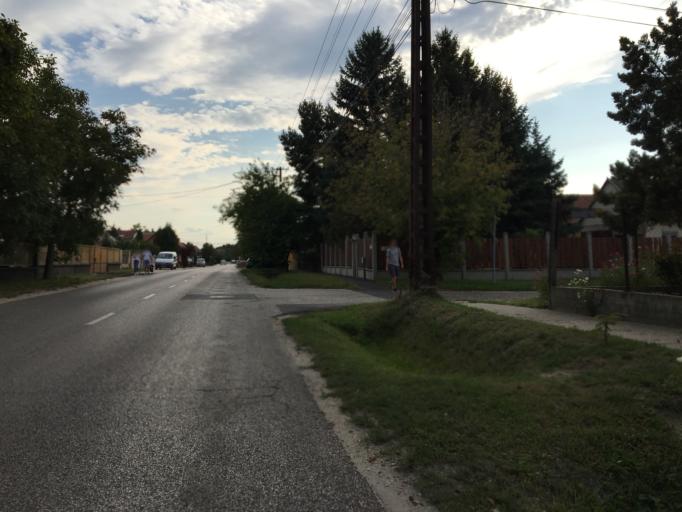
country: HU
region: Pest
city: Szigetszentmiklos
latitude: 47.3488
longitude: 19.0248
